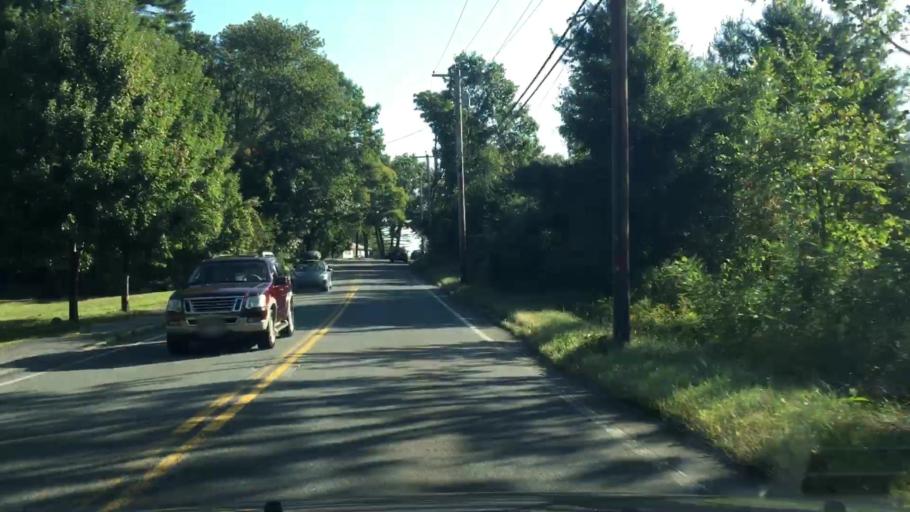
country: US
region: Massachusetts
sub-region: Essex County
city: Methuen
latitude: 42.6974
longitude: -71.2405
